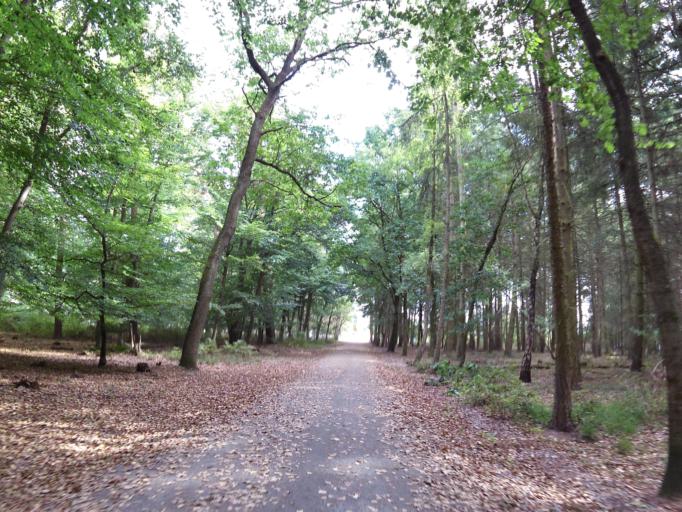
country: DE
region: Hesse
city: Morfelden-Walldorf
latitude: 50.0030
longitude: 8.5635
